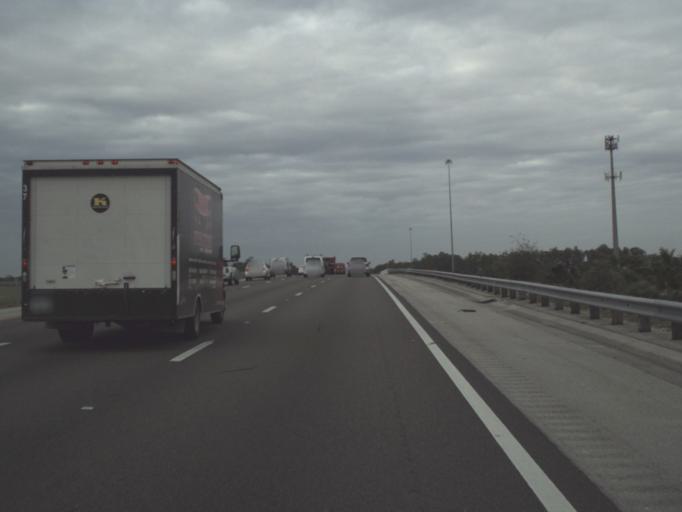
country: US
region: Florida
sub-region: Collier County
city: Vineyards
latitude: 26.2745
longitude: -81.7429
